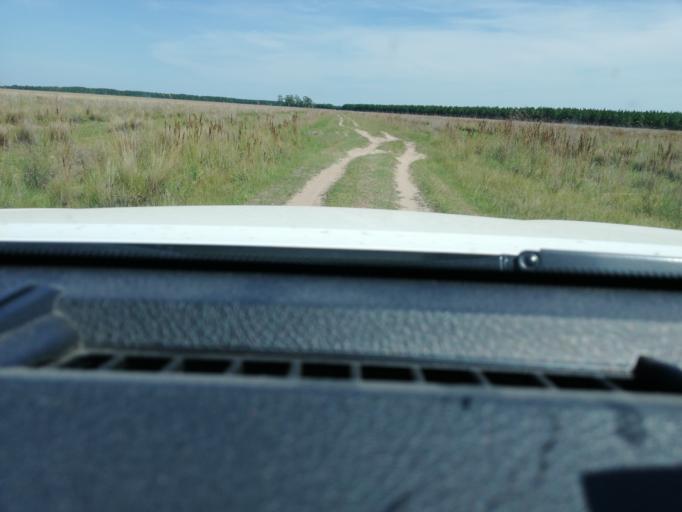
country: AR
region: Corrientes
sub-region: Departamento de San Miguel
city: San Miguel
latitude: -28.0436
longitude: -57.4579
